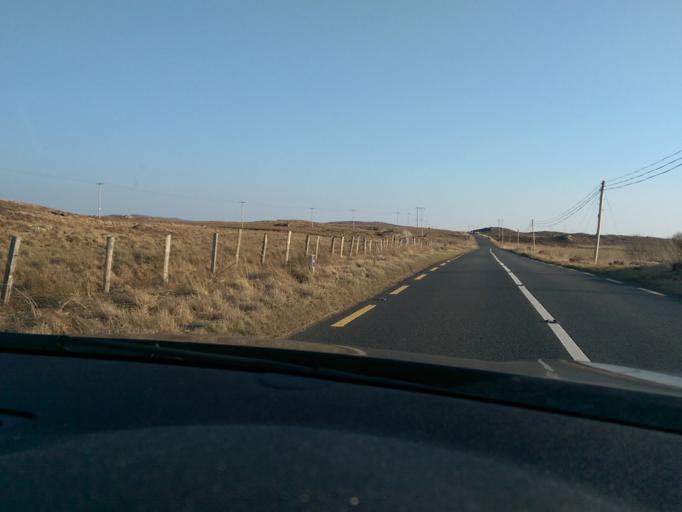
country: IE
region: Connaught
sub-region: County Galway
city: Oughterard
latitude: 53.3625
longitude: -9.5429
